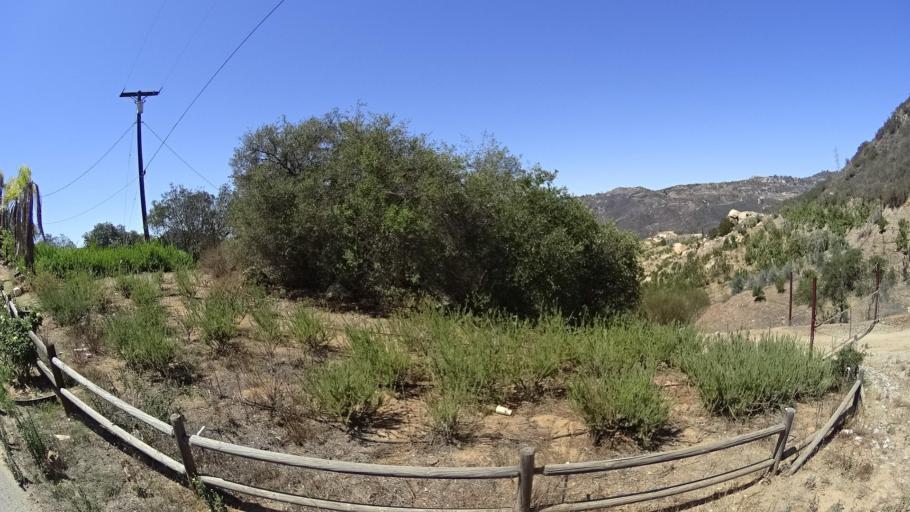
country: US
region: California
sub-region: San Diego County
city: Rainbow
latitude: 33.3862
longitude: -117.0999
